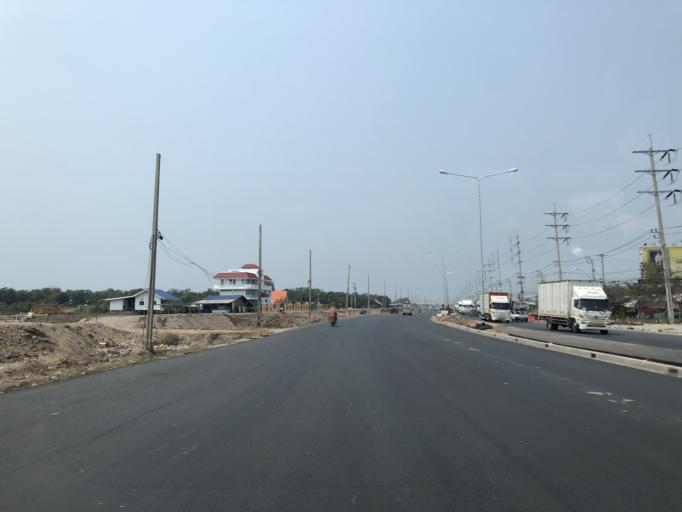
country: TH
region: Samut Prakan
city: Bang Bo
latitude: 13.5096
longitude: 100.8069
